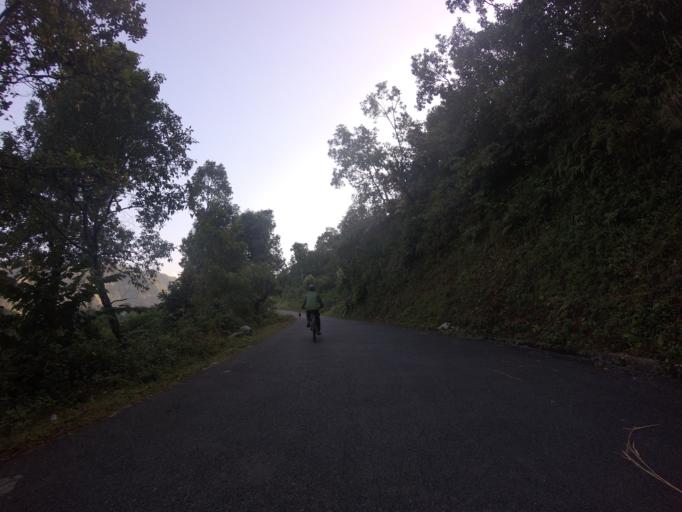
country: NP
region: Western Region
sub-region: Gandaki Zone
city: Pokhara
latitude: 28.2439
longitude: 84.0011
